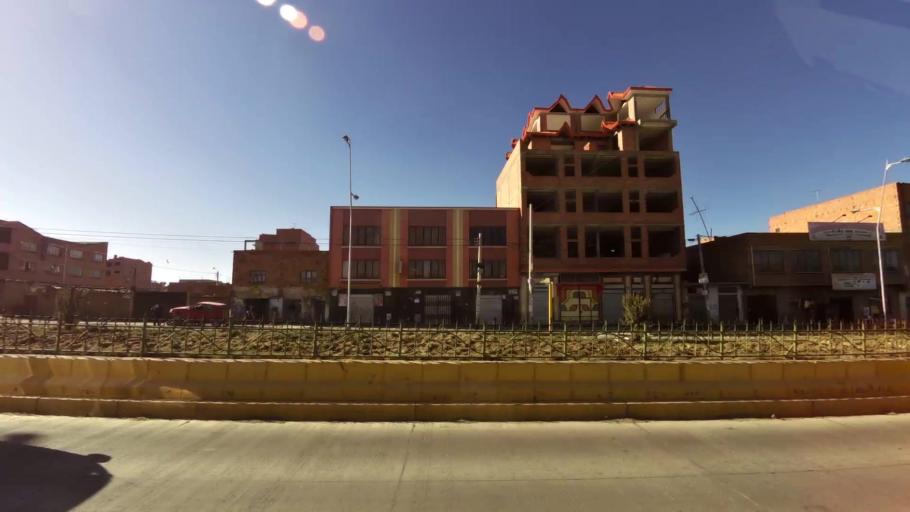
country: BO
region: La Paz
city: La Paz
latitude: -16.5230
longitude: -68.1801
